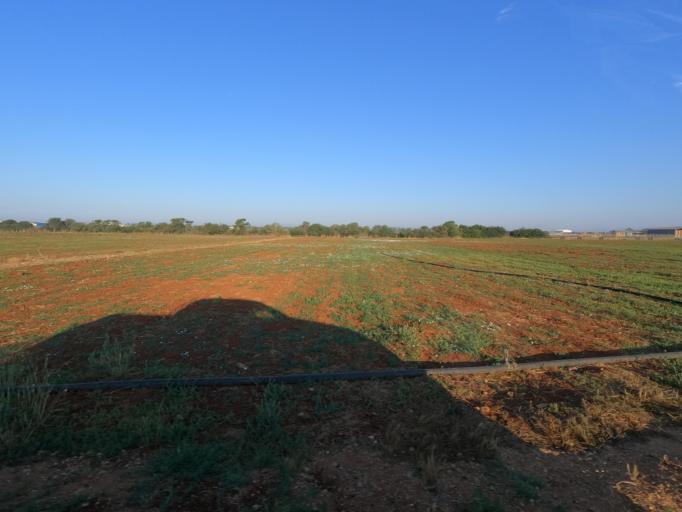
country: CY
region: Ammochostos
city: Achna
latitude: 35.0319
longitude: 33.7912
